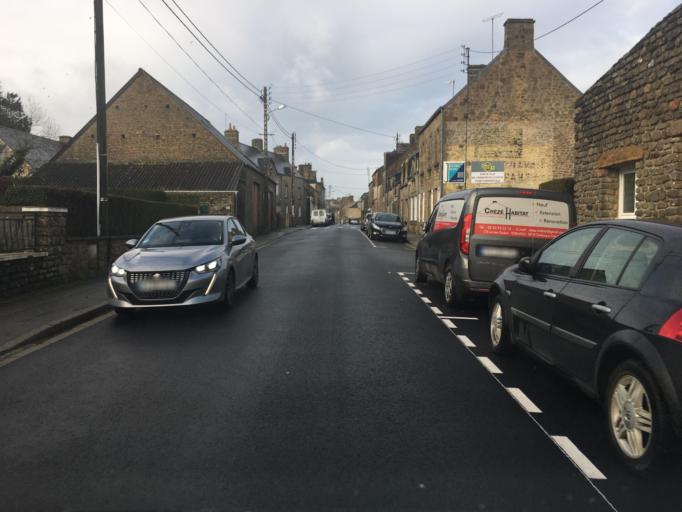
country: FR
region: Lower Normandy
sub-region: Departement de la Manche
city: Saint-Pierre-Eglise
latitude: 49.6671
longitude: -1.4003
